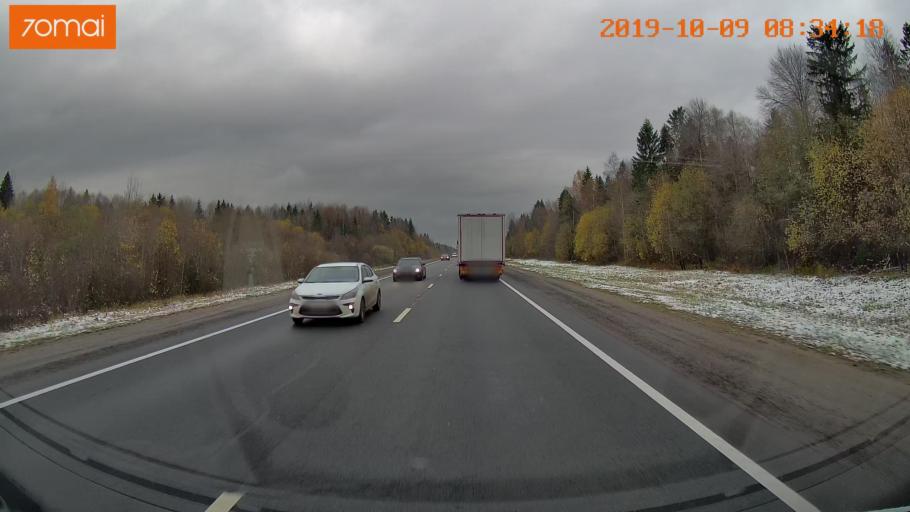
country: RU
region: Vologda
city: Gryazovets
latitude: 58.8951
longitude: 40.1863
